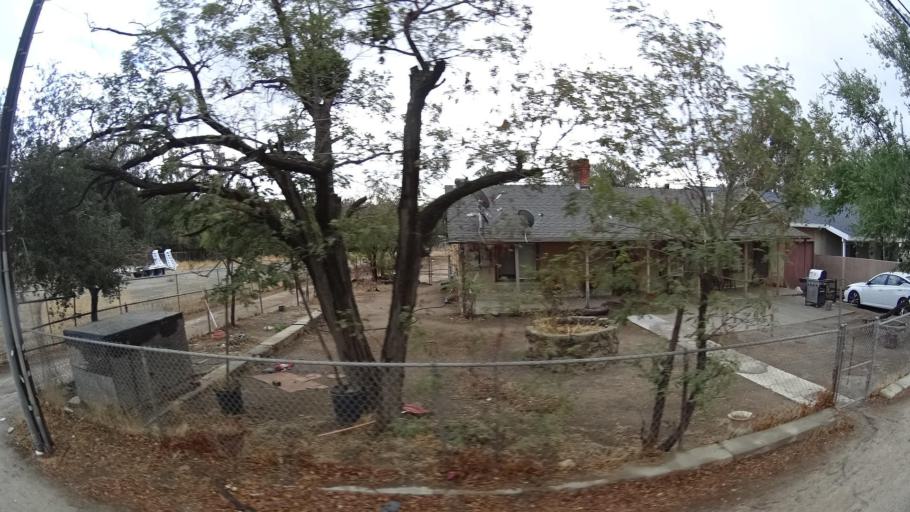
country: MX
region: Baja California
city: Tecate
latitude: 32.5822
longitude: -116.6212
